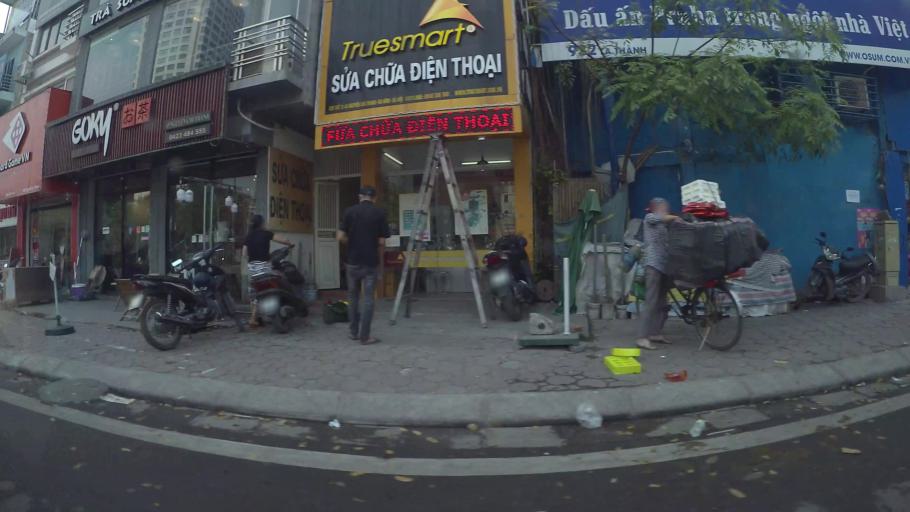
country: VN
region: Ha Noi
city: Cau Giay
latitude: 21.0249
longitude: 105.8116
